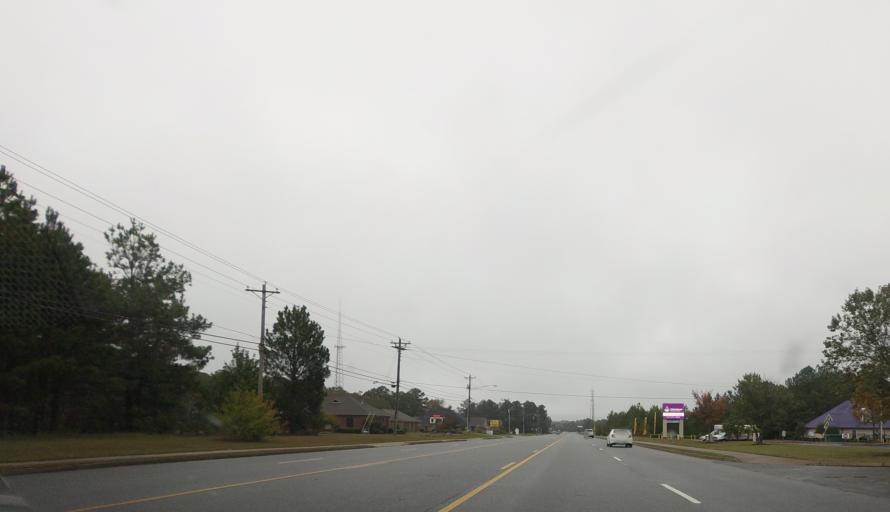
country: US
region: Georgia
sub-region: Houston County
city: Centerville
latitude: 32.5989
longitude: -83.6651
